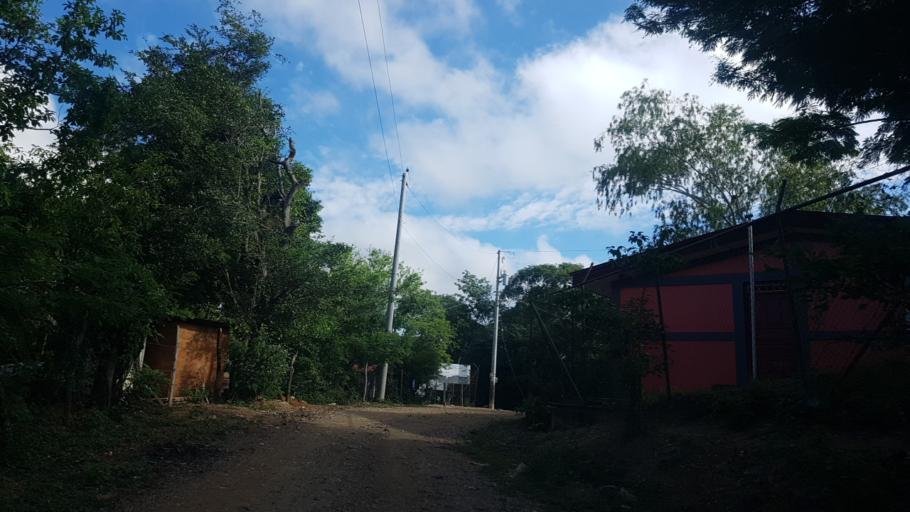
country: NI
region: Nueva Segovia
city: Ocotal
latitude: 13.6120
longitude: -86.4492
